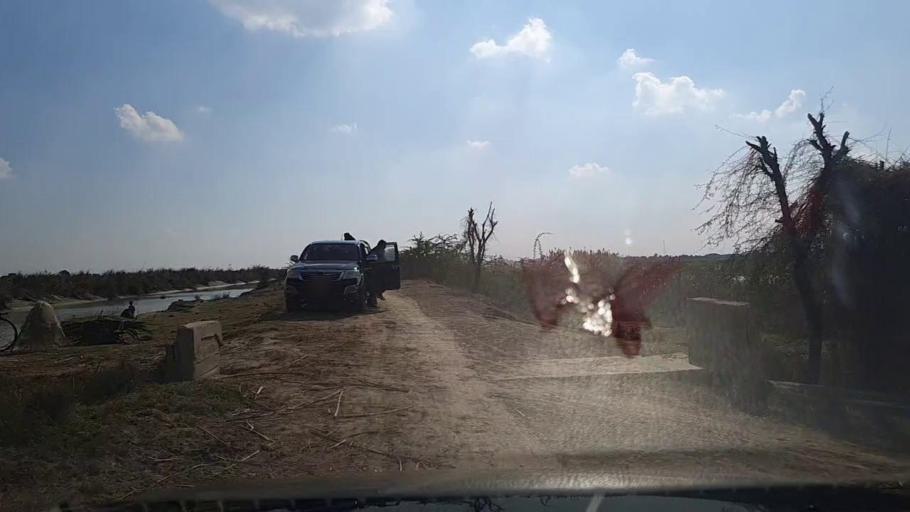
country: PK
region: Sindh
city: Tando Mittha Khan
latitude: 25.8455
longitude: 69.0743
